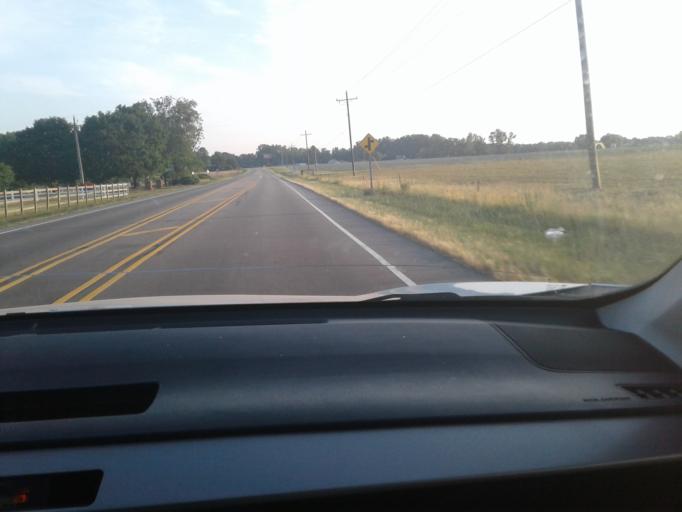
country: US
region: North Carolina
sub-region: Harnett County
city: Lillington
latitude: 35.4522
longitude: -78.8290
